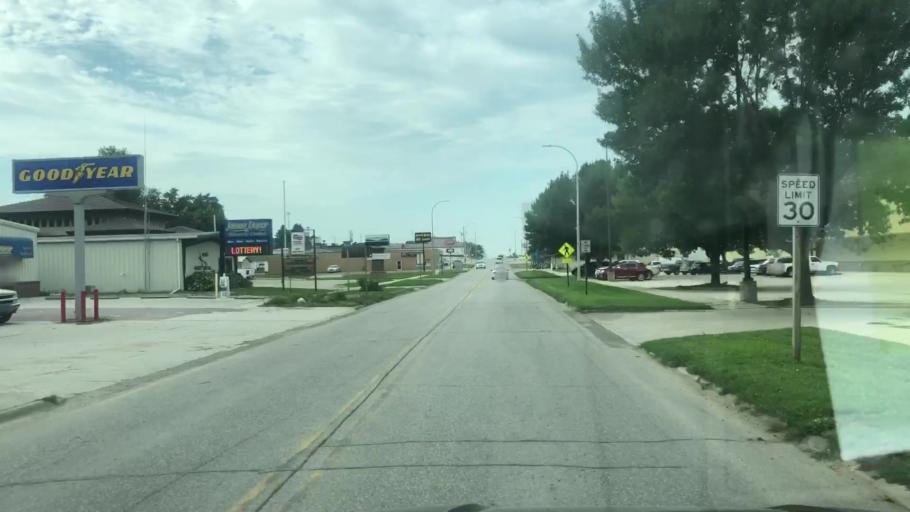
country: US
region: Iowa
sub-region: O'Brien County
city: Sheldon
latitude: 43.1846
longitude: -95.8548
